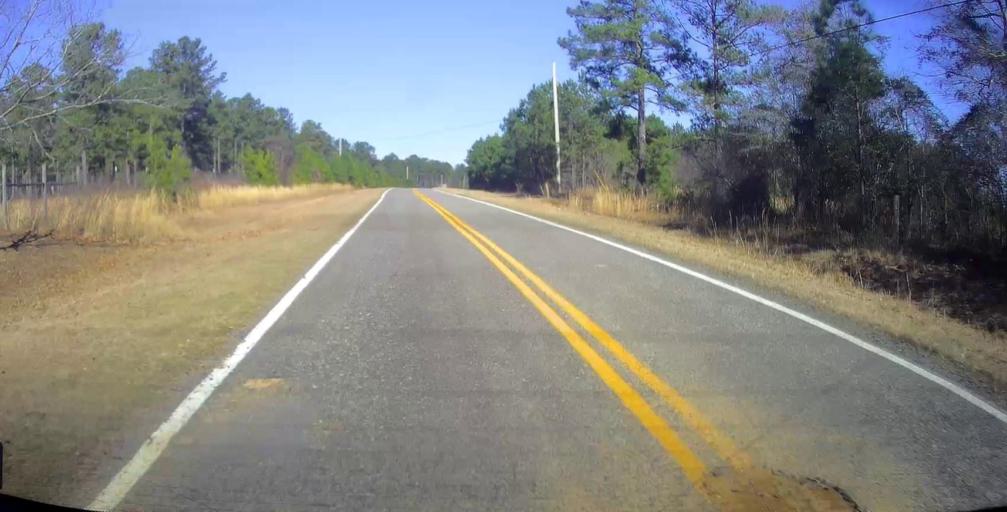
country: US
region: Georgia
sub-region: Peach County
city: Fort Valley
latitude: 32.6339
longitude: -83.9390
